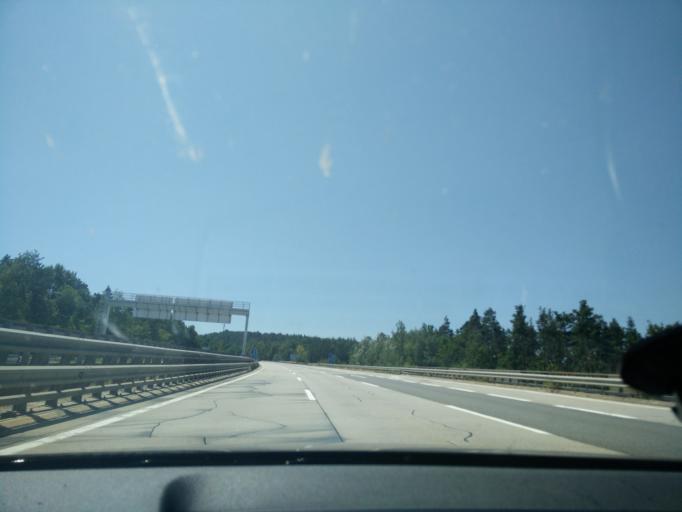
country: AT
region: Lower Austria
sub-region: Politischer Bezirk Neunkirchen
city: Breitenau
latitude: 47.7125
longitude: 16.1297
